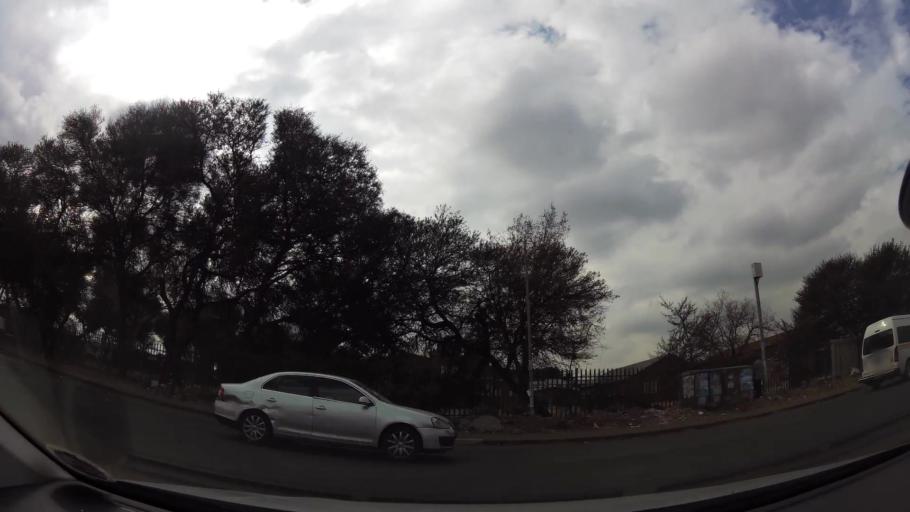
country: ZA
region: Gauteng
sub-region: City of Johannesburg Metropolitan Municipality
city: Soweto
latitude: -26.2708
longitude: 27.8554
